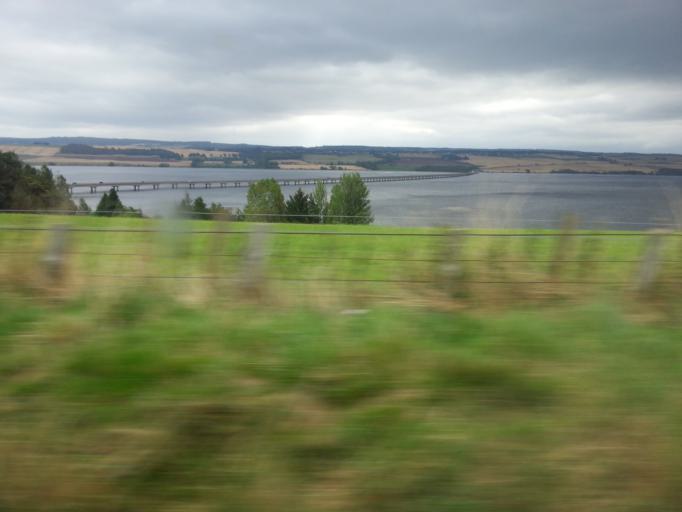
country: GB
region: Scotland
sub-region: Highland
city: Evanton
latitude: 57.6275
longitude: -4.3743
